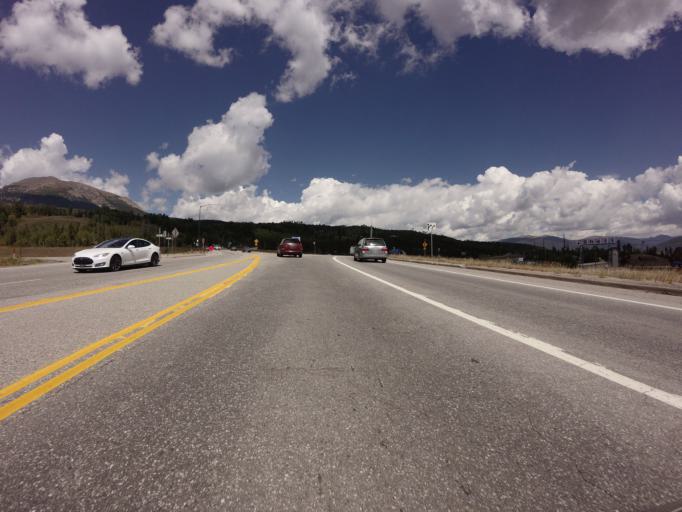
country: US
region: Colorado
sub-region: Summit County
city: Frisco
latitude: 39.5919
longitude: -106.0957
